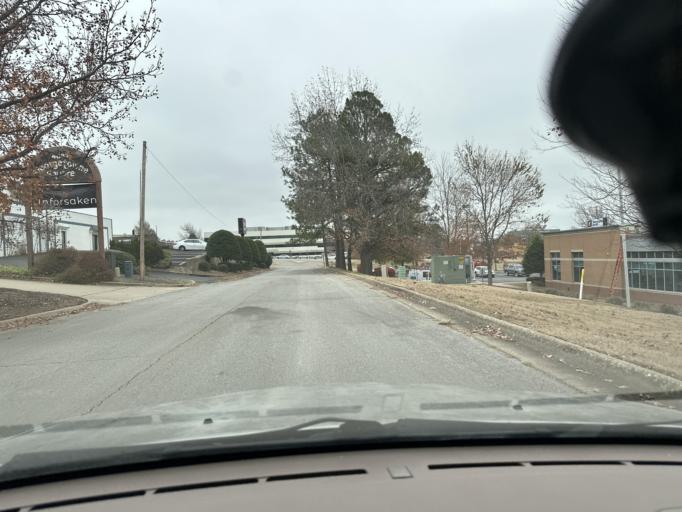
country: US
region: Arkansas
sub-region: Washington County
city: Johnson
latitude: 36.1248
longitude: -94.1464
